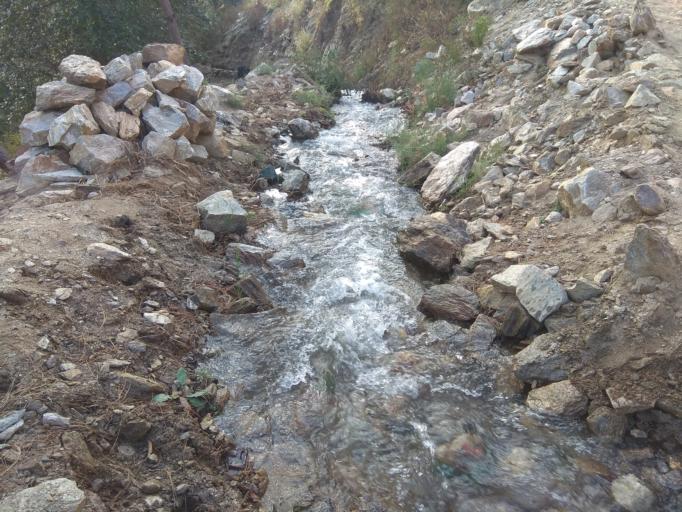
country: NP
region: Mid Western
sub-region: Bheri Zone
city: Dailekh
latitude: 29.2484
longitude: 81.6591
